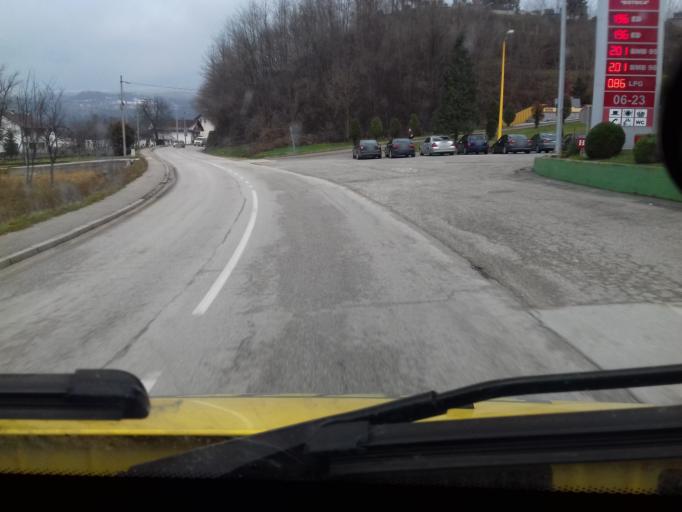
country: BA
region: Federation of Bosnia and Herzegovina
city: Zepce
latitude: 44.4201
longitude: 18.0739
